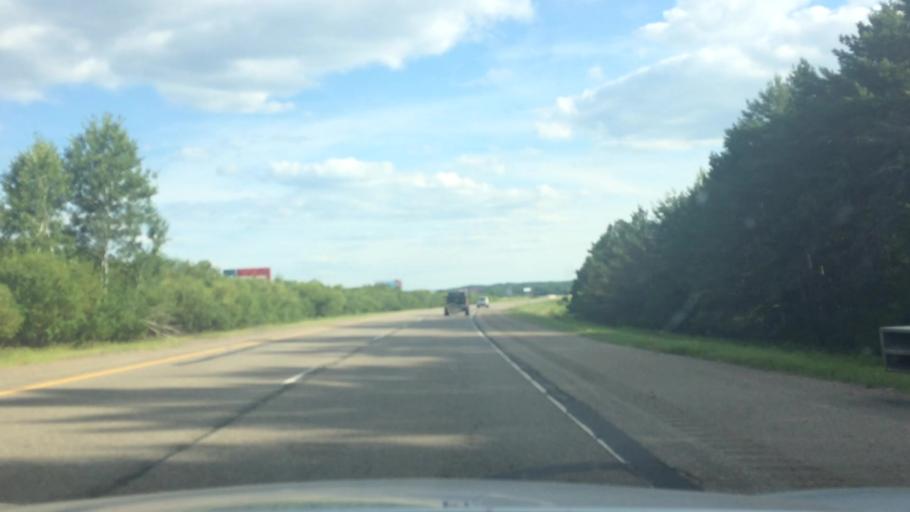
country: US
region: Wisconsin
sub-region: Lincoln County
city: Merrill
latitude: 45.1629
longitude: -89.6435
